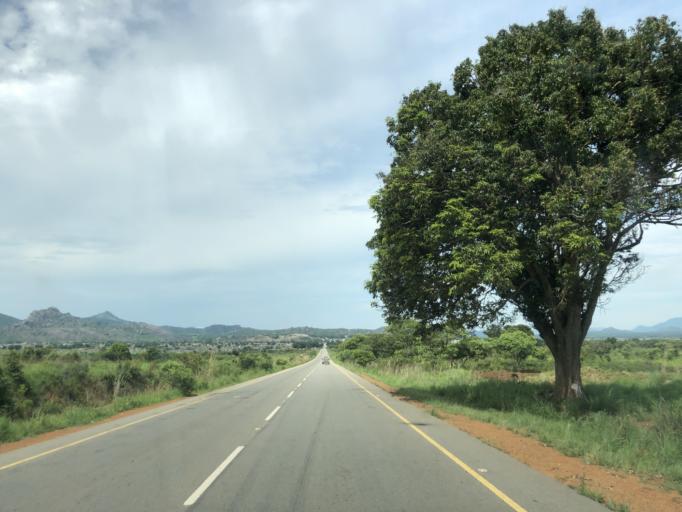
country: AO
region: Cuanza Sul
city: Quibala
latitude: -10.7341
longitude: 15.0095
